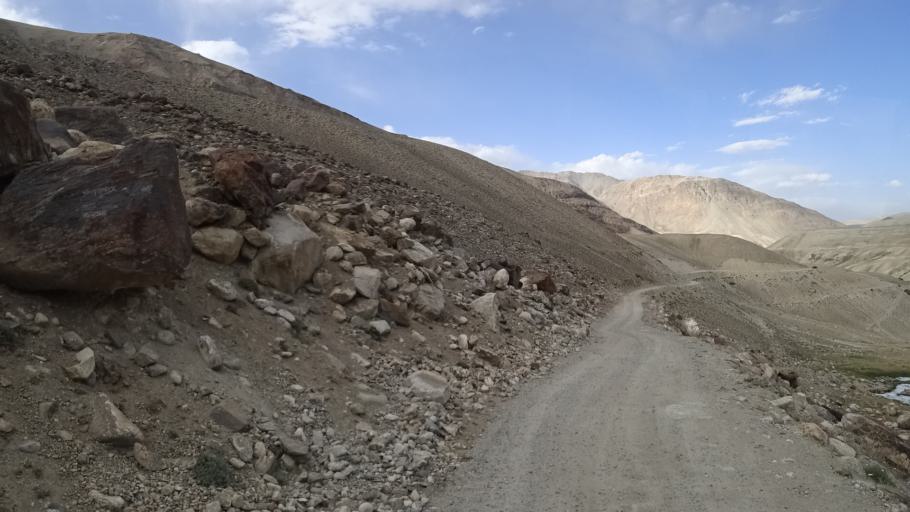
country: AF
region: Badakhshan
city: Khandud
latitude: 37.2202
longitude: 72.7873
